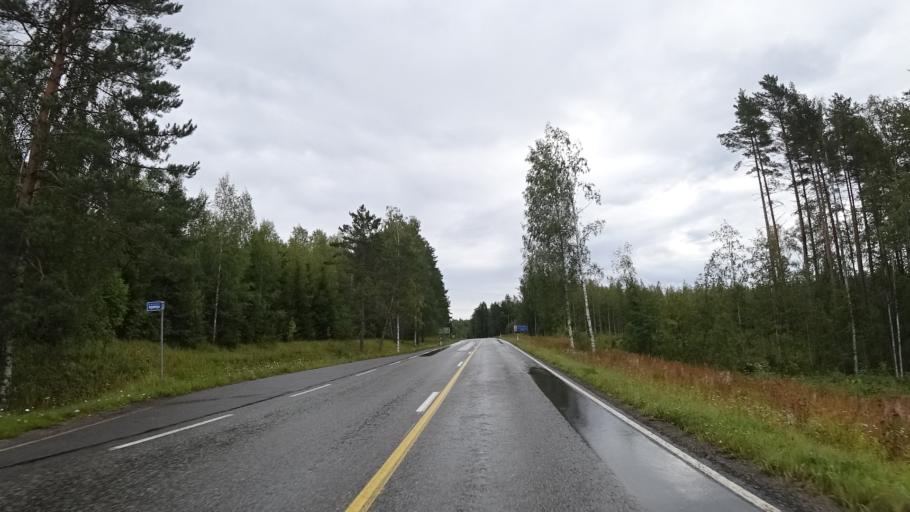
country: FI
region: Southern Savonia
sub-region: Savonlinna
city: Kerimaeki
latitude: 62.0360
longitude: 29.5289
